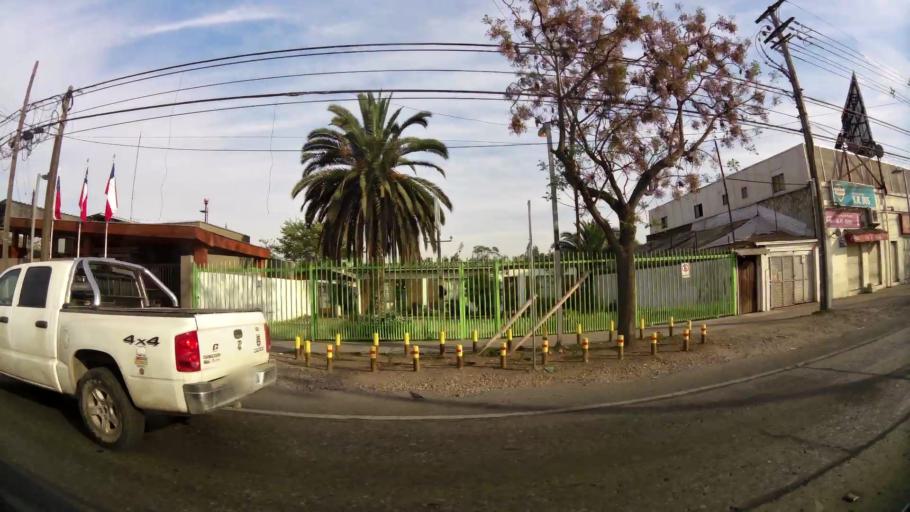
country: CL
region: Santiago Metropolitan
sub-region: Provincia de Talagante
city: Penaflor
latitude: -33.5688
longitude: -70.8149
